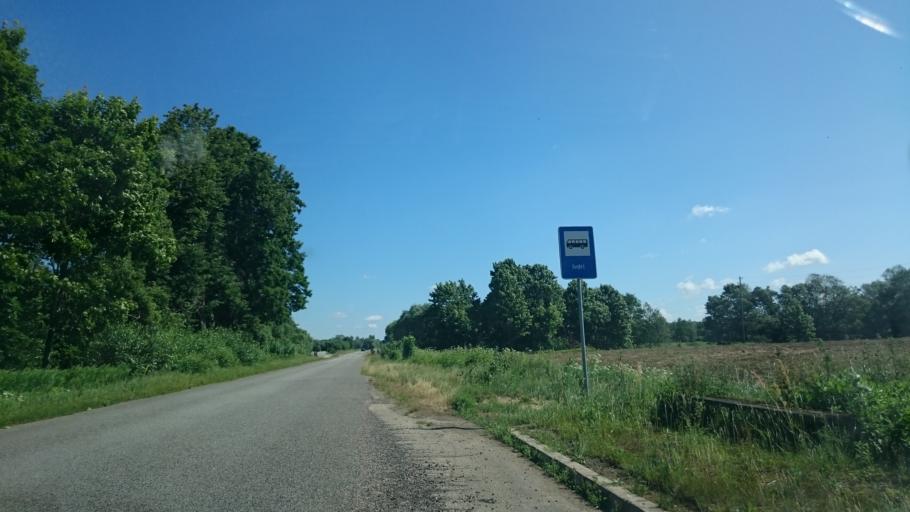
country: LV
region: Cibla
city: Cibla
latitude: 56.5157
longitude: 27.8003
